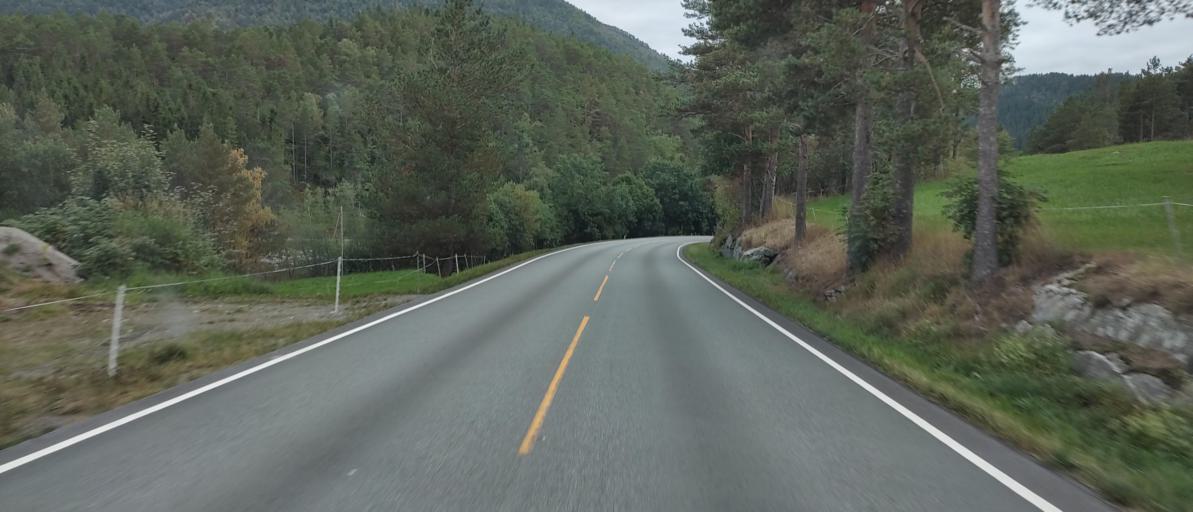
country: NO
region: More og Romsdal
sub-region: Rauma
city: Andalsnes
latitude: 62.5773
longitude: 7.5461
